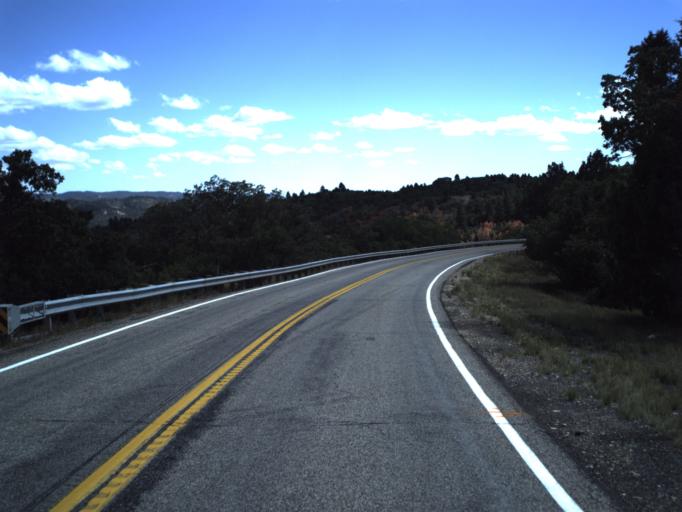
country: US
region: Utah
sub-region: Garfield County
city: Panguitch
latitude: 37.4954
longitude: -112.5307
